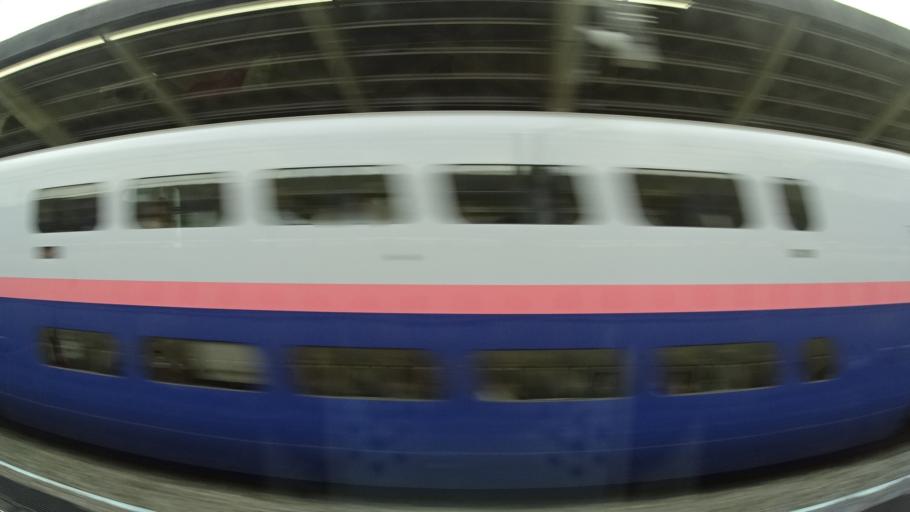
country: JP
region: Saitama
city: Kumagaya
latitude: 36.1397
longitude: 139.3888
